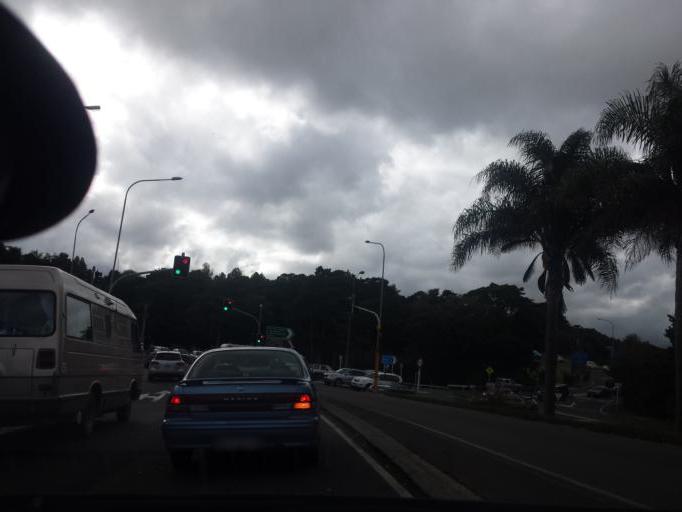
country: NZ
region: Auckland
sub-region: Auckland
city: Warkworth
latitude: -36.3974
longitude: 174.6608
